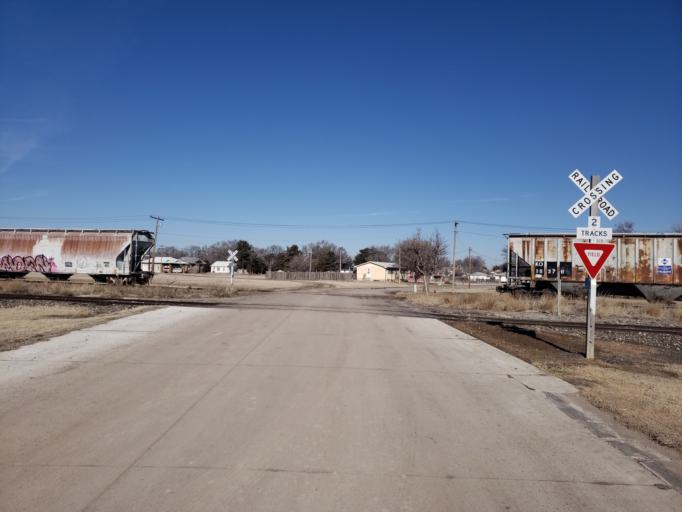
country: US
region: Kansas
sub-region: Ness County
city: Ness City
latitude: 38.4454
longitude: -99.6904
